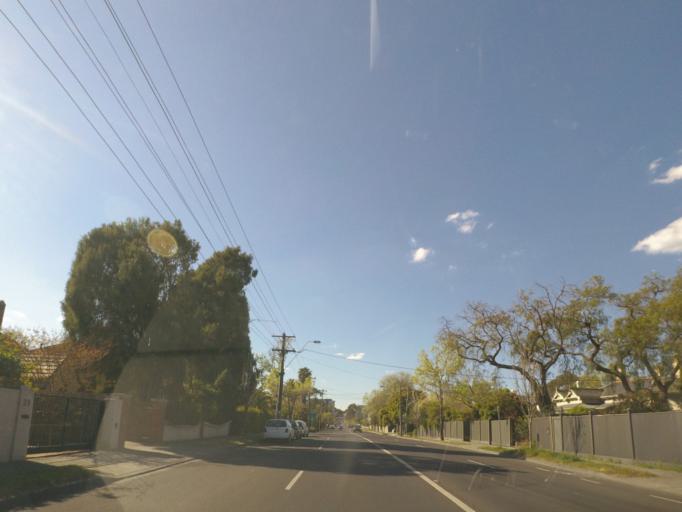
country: AU
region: Victoria
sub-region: Boroondara
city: Kew
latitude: -37.8157
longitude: 145.0274
